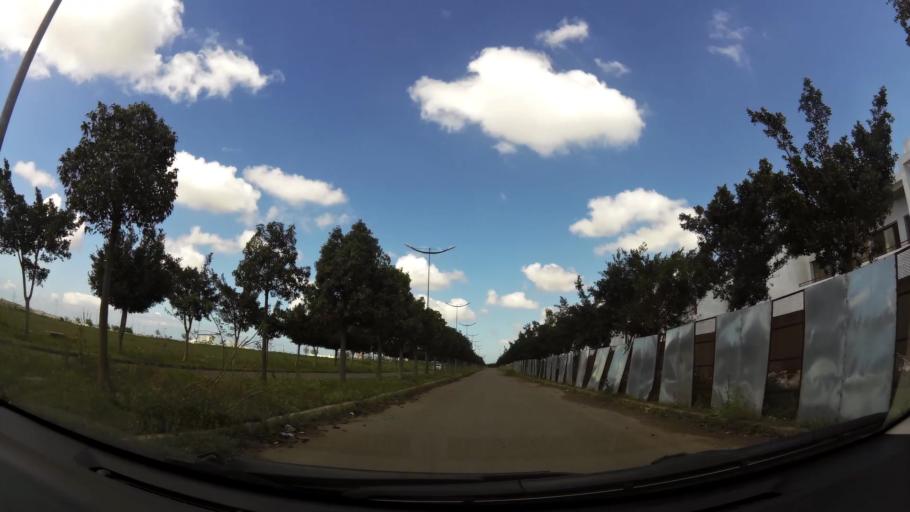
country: MA
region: Grand Casablanca
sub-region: Nouaceur
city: Dar Bouazza
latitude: 33.4186
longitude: -7.8271
